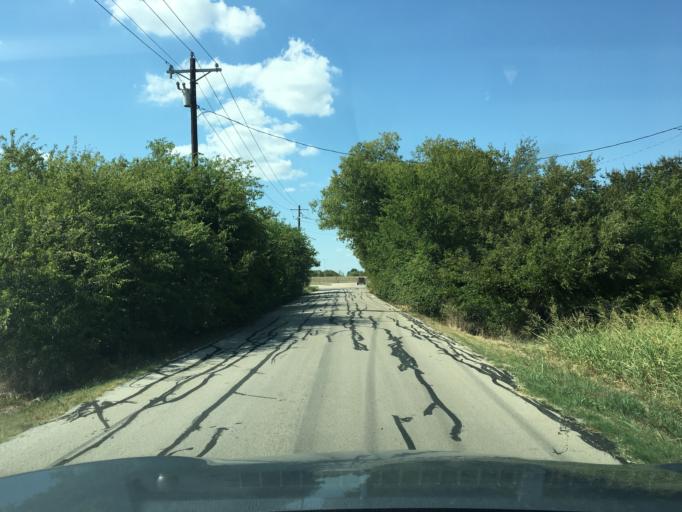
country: US
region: Texas
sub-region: Tarrant County
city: Mansfield
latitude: 32.5261
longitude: -97.0803
